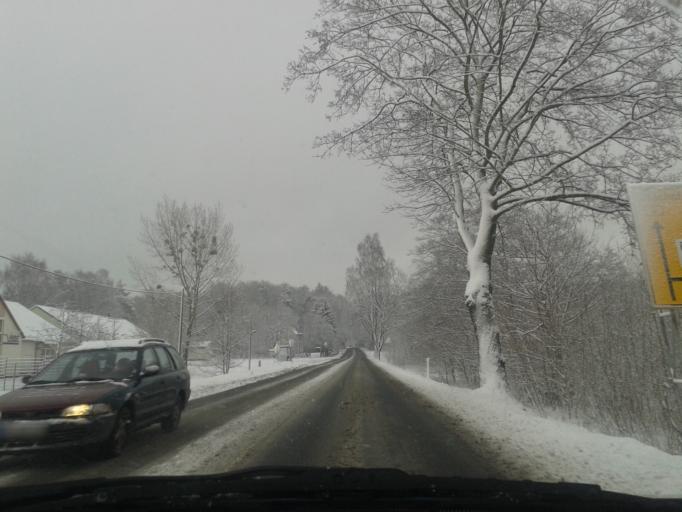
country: DE
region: Saxony
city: Radeberg
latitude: 51.0637
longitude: 13.9390
